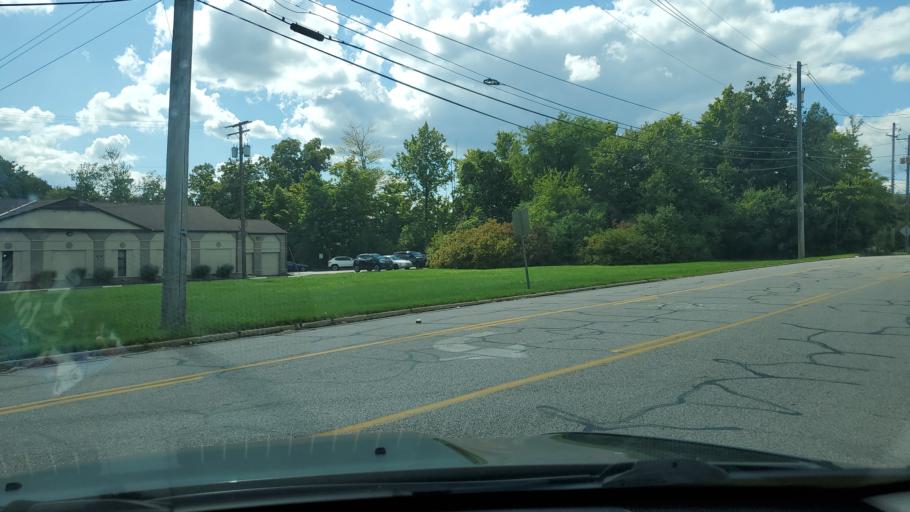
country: US
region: Ohio
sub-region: Mahoning County
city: Boardman
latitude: 41.0211
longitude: -80.6543
